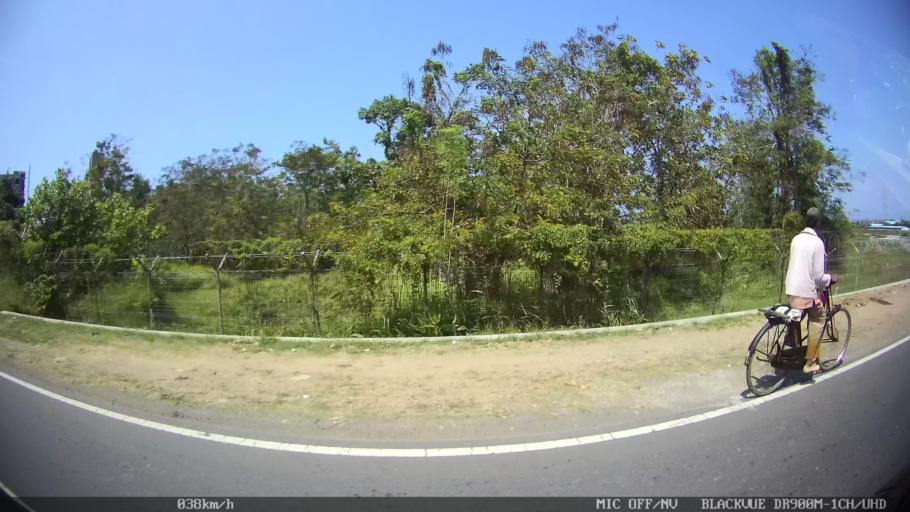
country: ID
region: Daerah Istimewa Yogyakarta
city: Srandakan
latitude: -7.8865
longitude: 110.0687
